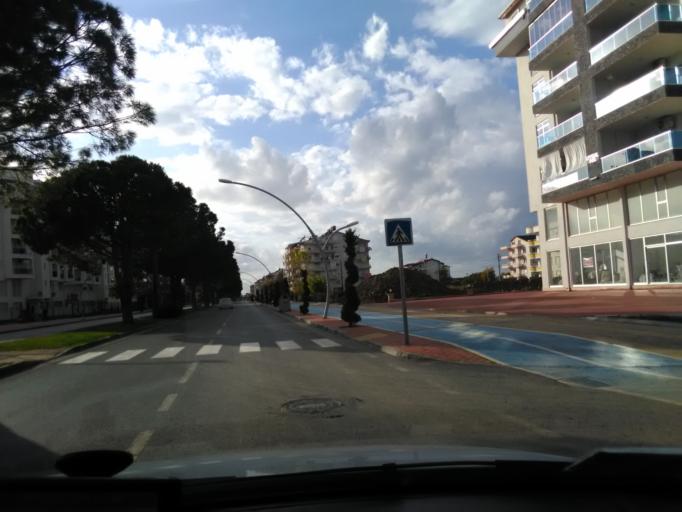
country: TR
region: Antalya
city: Gazipasa
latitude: 36.2659
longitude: 32.2961
